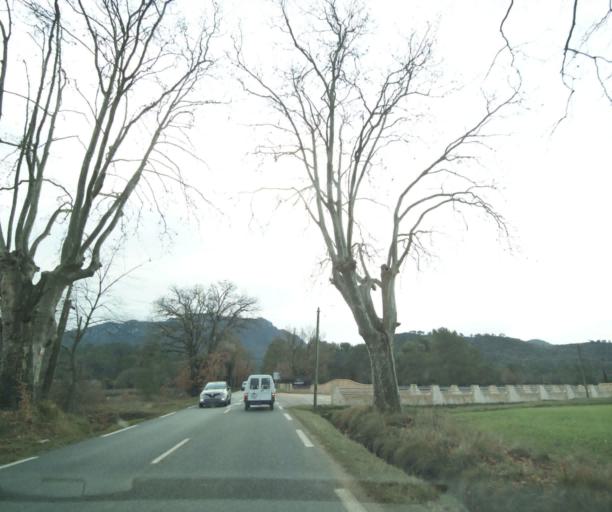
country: FR
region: Provence-Alpes-Cote d'Azur
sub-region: Departement du Var
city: La Roquebrussanne
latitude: 43.3916
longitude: 5.9756
